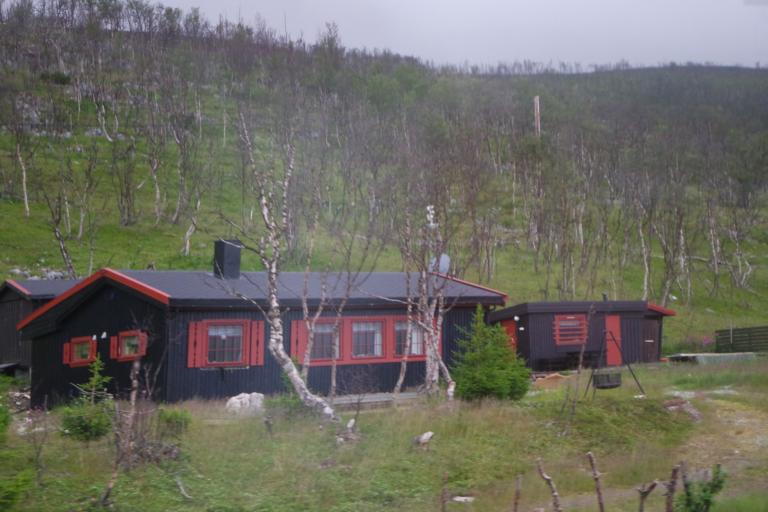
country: NO
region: Finnmark Fylke
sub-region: Kvalsund
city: Kvalsund
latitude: 70.3234
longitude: 24.2458
